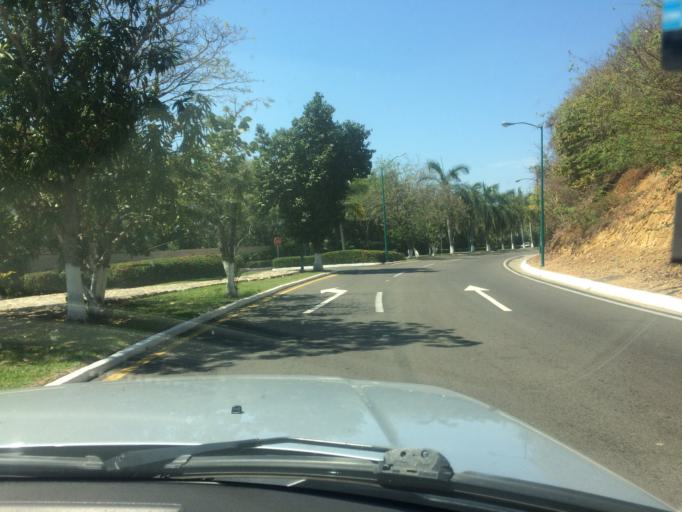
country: MX
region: Guerrero
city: Ixtapa
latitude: 17.6670
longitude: -101.6285
